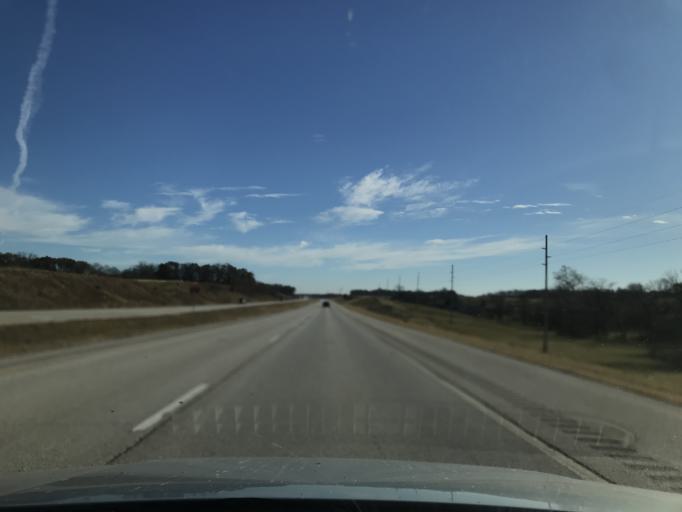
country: US
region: Illinois
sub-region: Hancock County
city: Carthage
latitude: 40.4145
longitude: -91.0340
